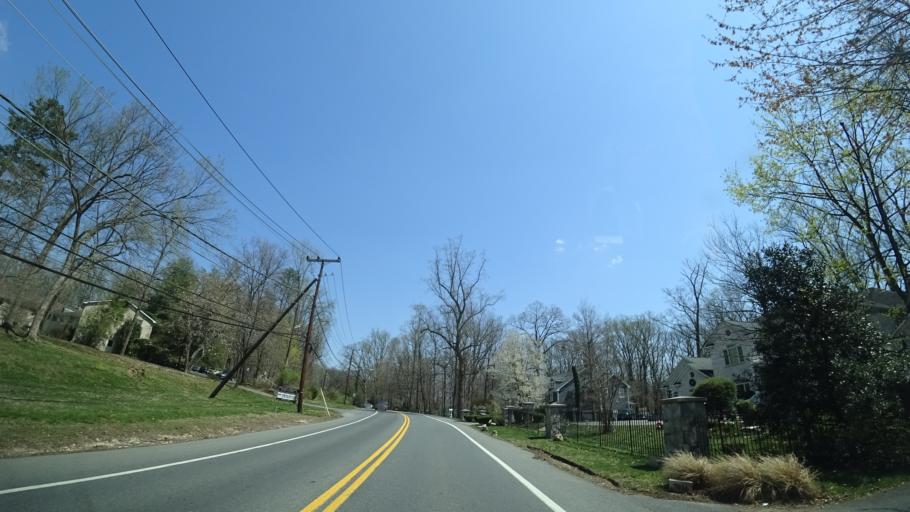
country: US
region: Maryland
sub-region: Montgomery County
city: Cabin John
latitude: 39.0050
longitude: -77.1447
